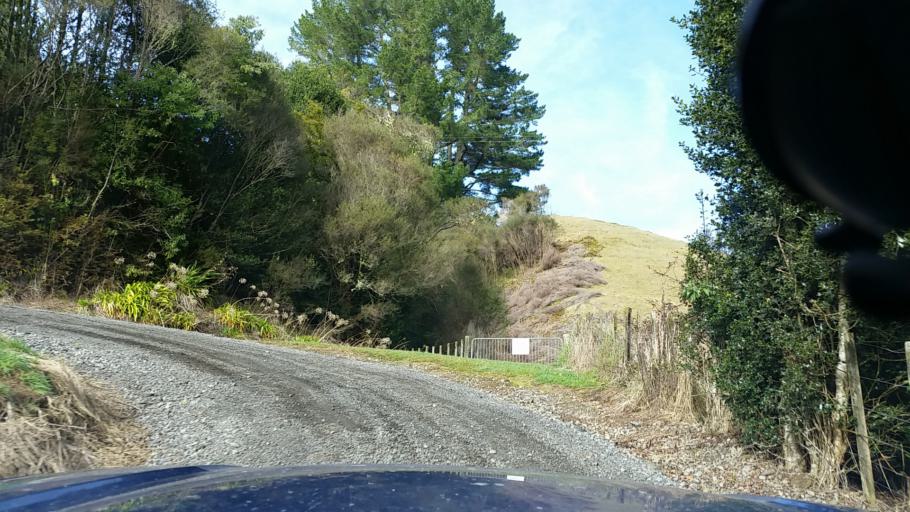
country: NZ
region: Taranaki
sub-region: New Plymouth District
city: Waitara
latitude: -39.0337
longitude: 174.8009
